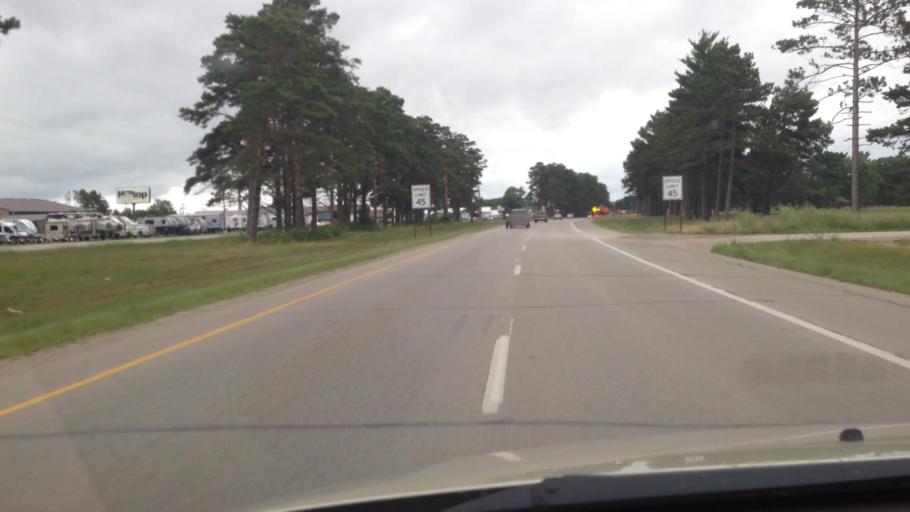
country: US
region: Michigan
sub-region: Delta County
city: Escanaba
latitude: 45.7822
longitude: -87.0829
